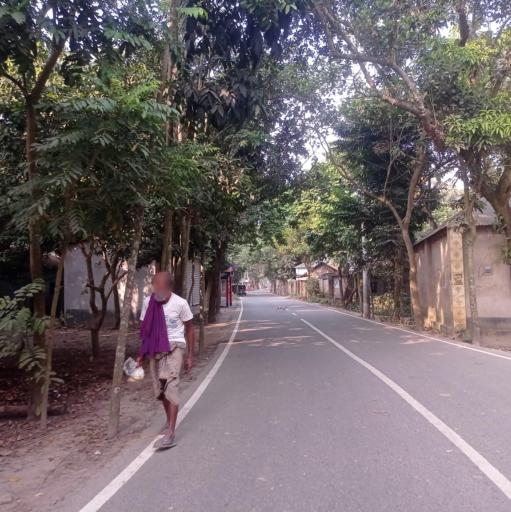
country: BD
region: Dhaka
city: Bhairab Bazar
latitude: 24.0959
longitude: 90.8530
